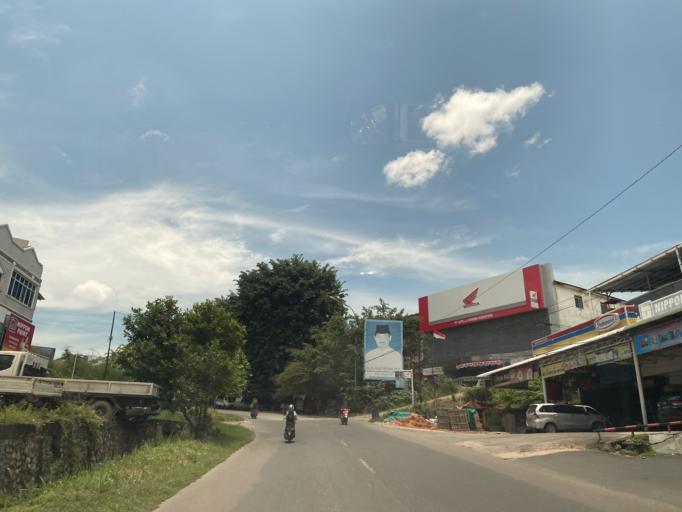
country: SG
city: Singapore
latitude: 1.1556
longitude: 104.0240
